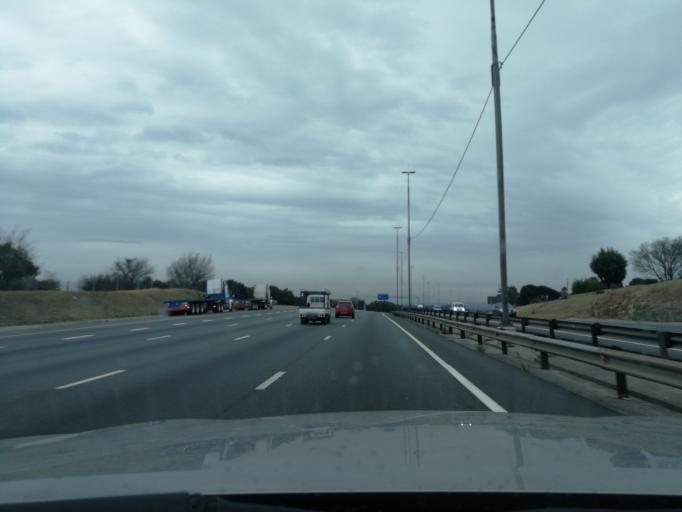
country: ZA
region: Gauteng
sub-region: Ekurhuleni Metropolitan Municipality
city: Germiston
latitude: -26.2595
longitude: 28.1508
